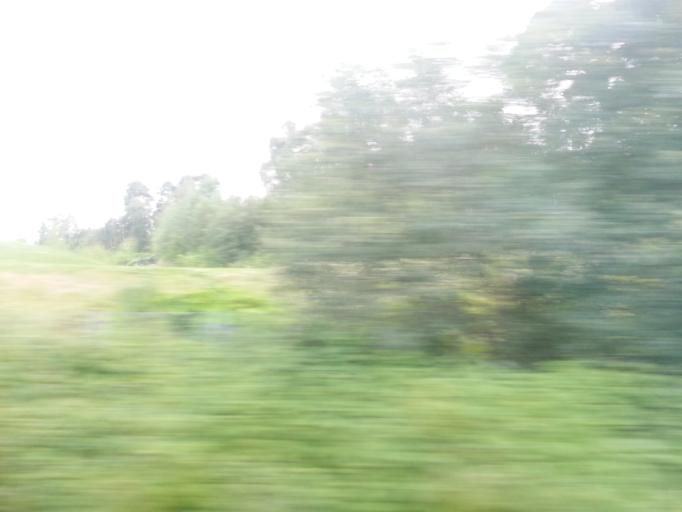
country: NO
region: Sor-Trondelag
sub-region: Trondheim
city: Trondheim
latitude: 63.4320
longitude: 10.5044
